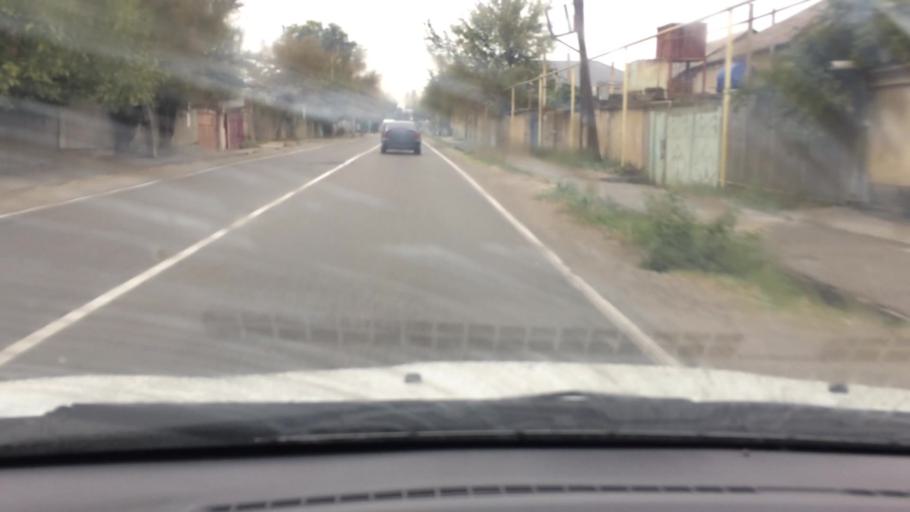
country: GE
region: Kvemo Kartli
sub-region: Marneuli
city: Marneuli
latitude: 41.4810
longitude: 44.8002
